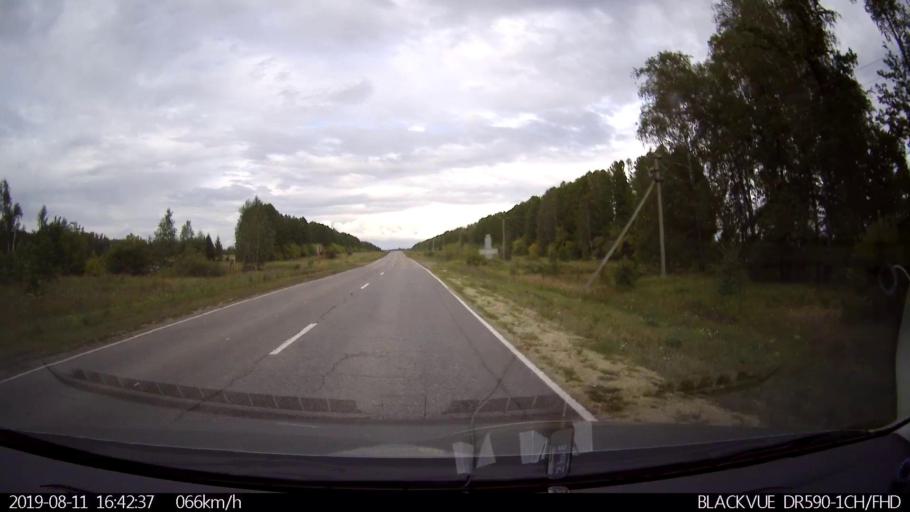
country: RU
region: Ulyanovsk
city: Mayna
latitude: 54.1620
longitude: 47.6641
